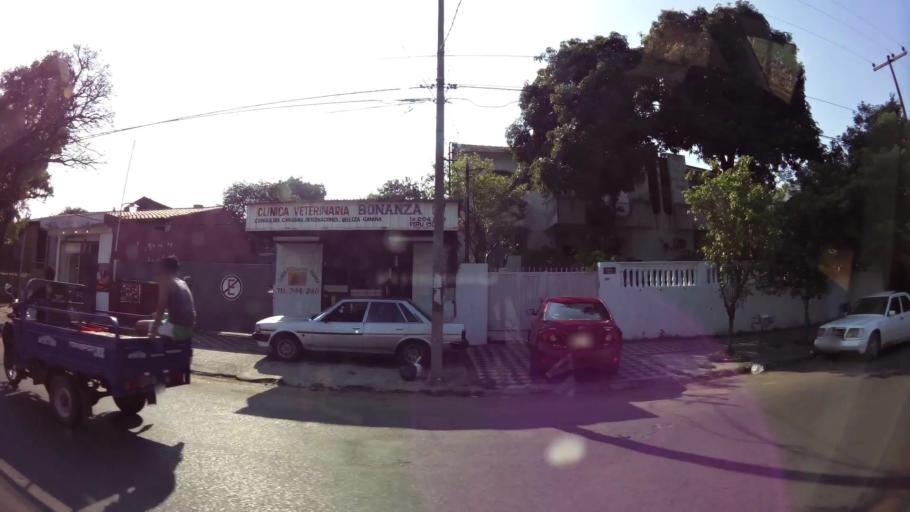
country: PY
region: Asuncion
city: Asuncion
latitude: -25.3017
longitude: -57.6283
